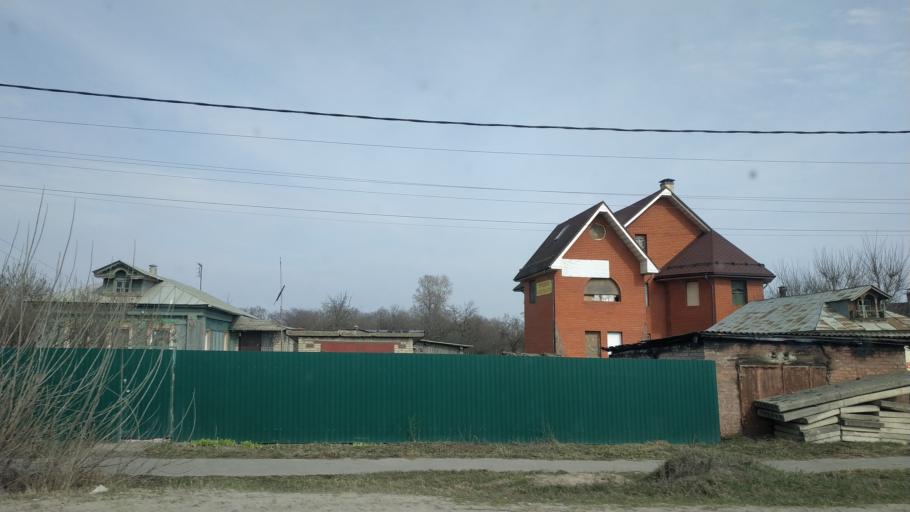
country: RU
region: Moskovskaya
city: Bronnitsy
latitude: 55.3968
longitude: 38.3198
